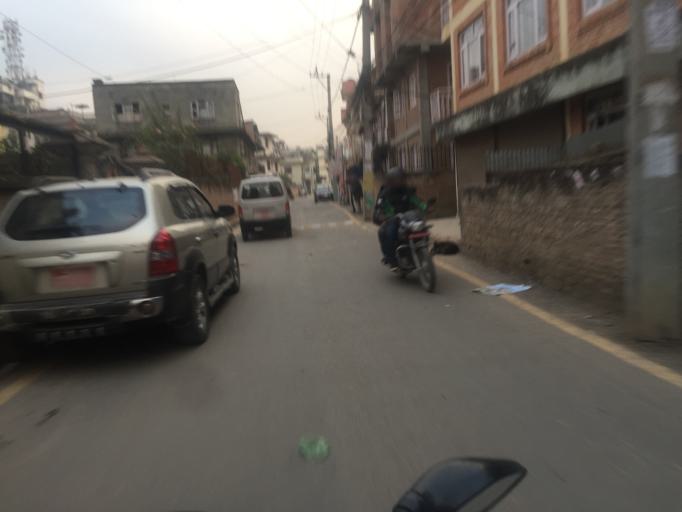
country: NP
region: Central Region
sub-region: Bagmati Zone
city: Patan
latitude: 27.6728
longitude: 85.3089
